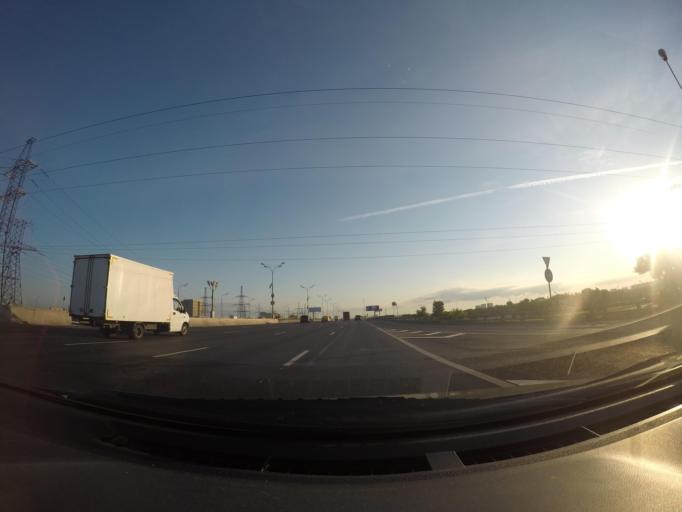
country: RU
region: Moscow
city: Zhulebino
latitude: 55.7070
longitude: 37.8348
